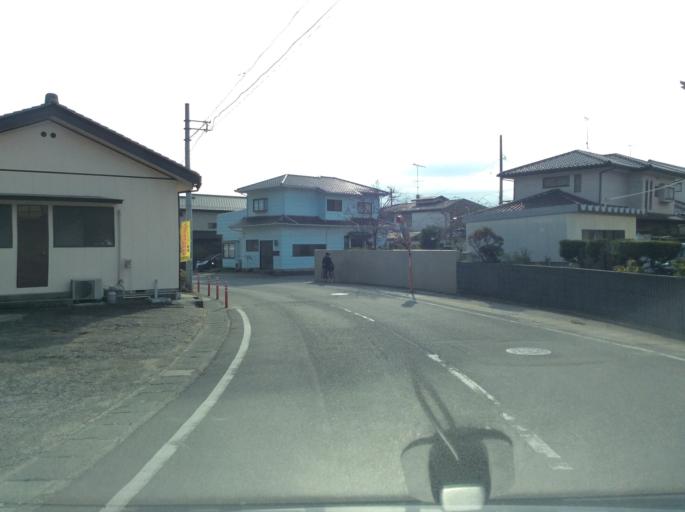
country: JP
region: Fukushima
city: Iwaki
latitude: 37.0701
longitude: 140.9427
